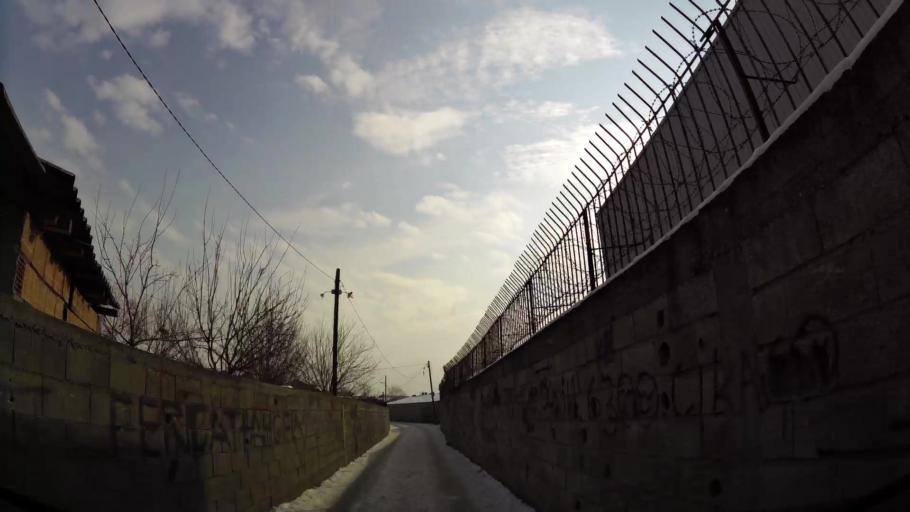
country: MK
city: Krushopek
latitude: 42.0157
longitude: 21.3839
